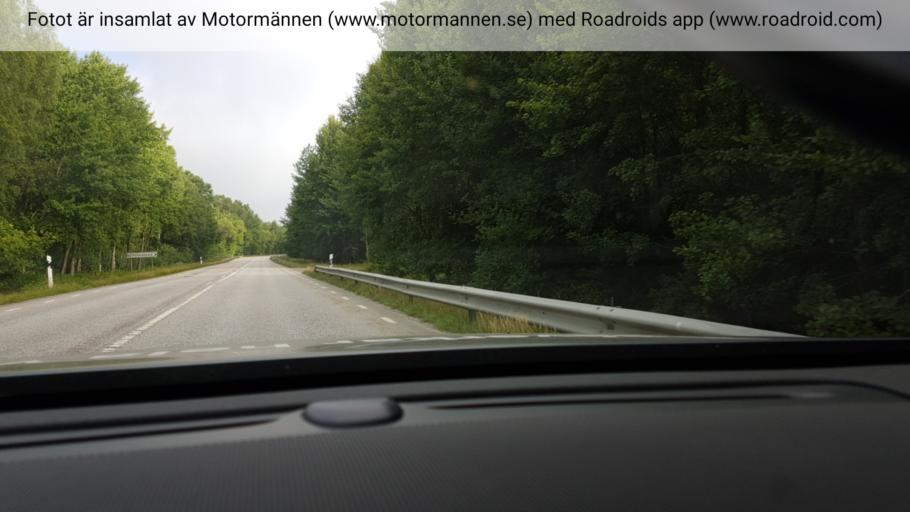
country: SE
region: Skane
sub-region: Hassleholms Kommun
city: Bjarnum
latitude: 56.2714
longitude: 13.7170
